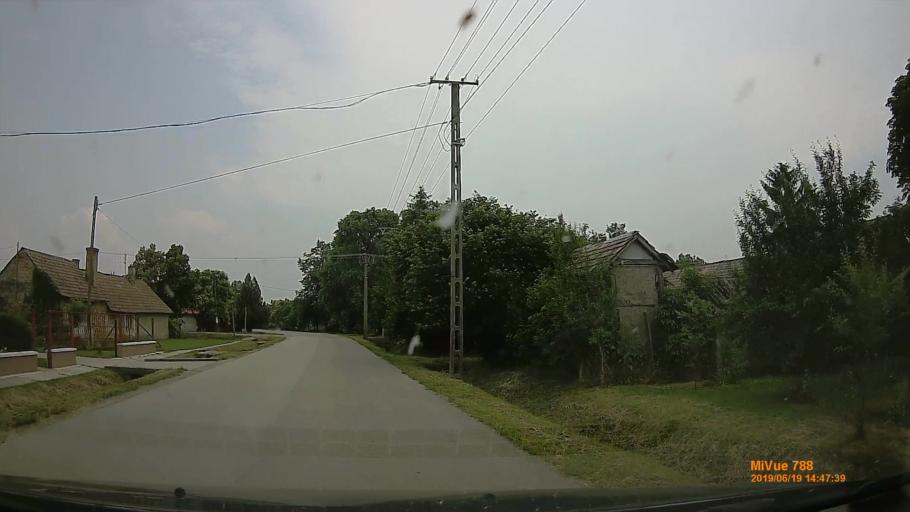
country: HU
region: Baranya
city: Szigetvar
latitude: 45.9958
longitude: 17.8317
